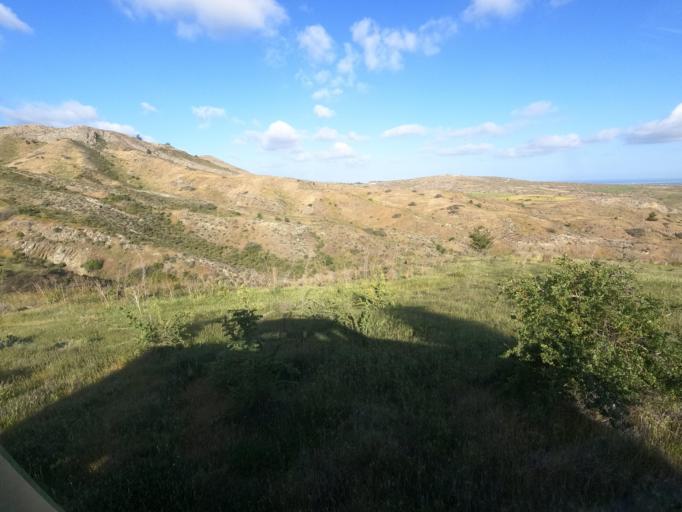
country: CY
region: Lefkosia
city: Astromeritis
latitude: 35.0739
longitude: 33.0397
